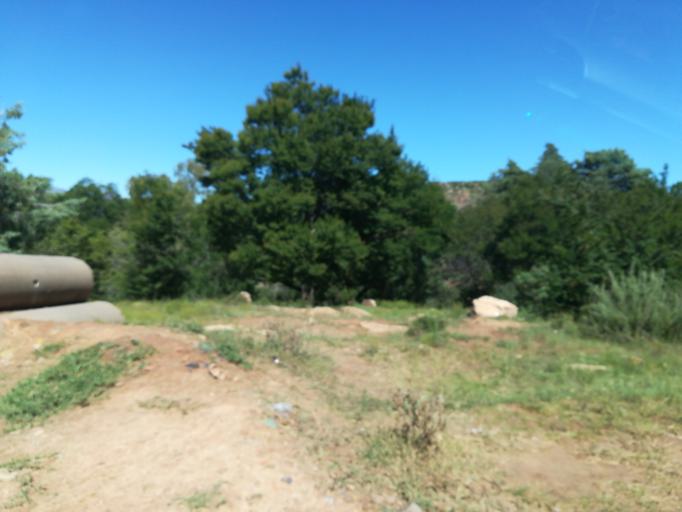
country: LS
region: Quthing
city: Quthing
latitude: -30.3399
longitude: 27.5450
